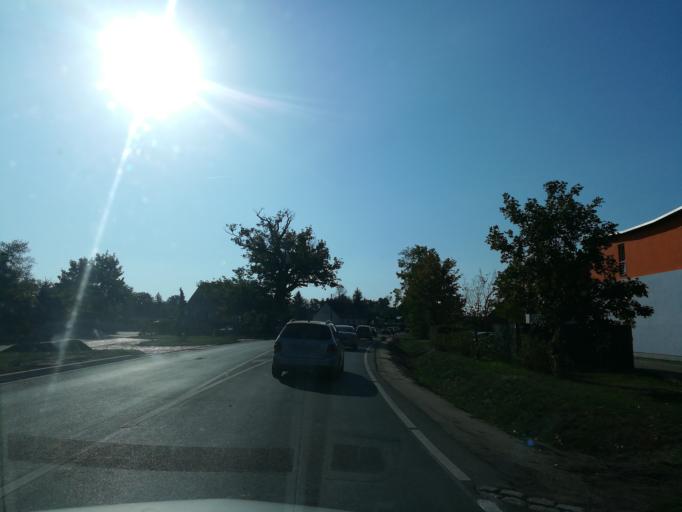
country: DE
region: Saxony-Anhalt
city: Wahlitz
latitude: 52.1080
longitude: 11.7812
